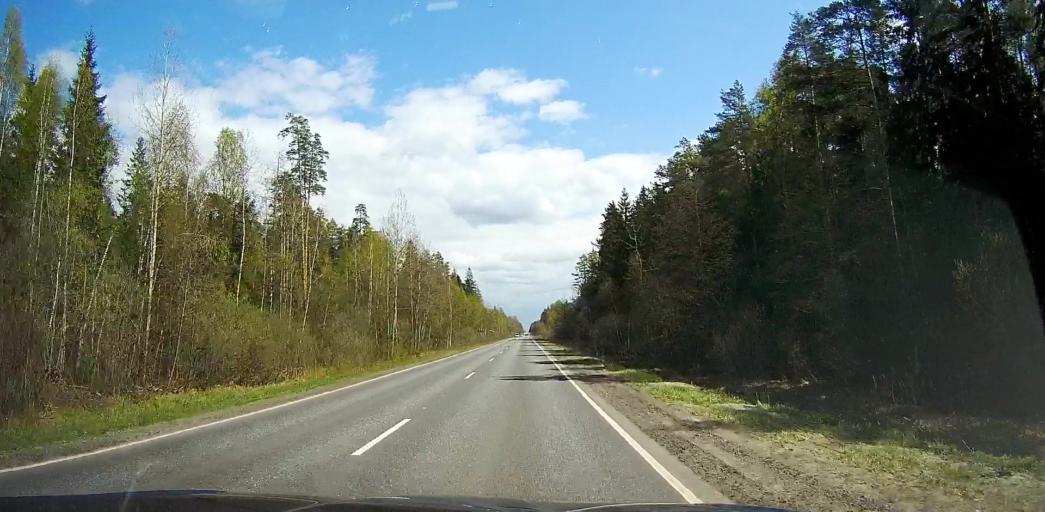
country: RU
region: Moskovskaya
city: Imeni Tsyurupy
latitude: 55.5513
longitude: 38.7315
